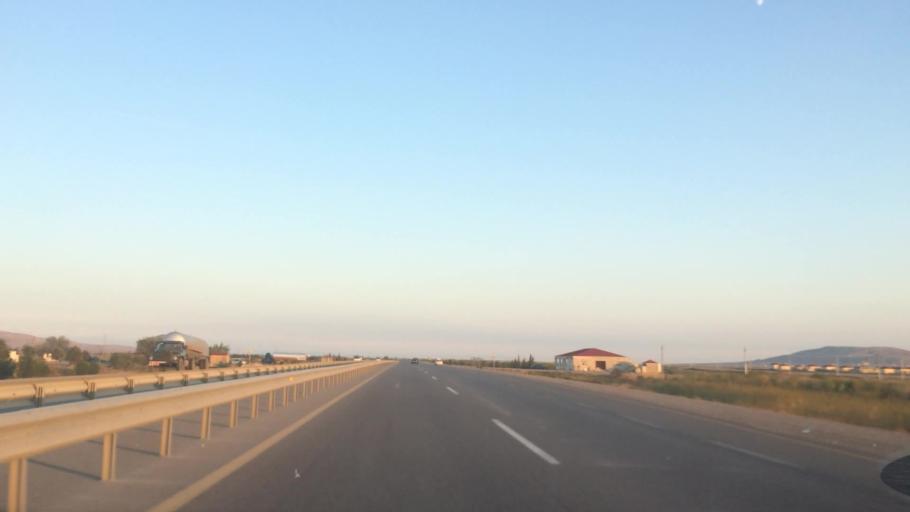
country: AZ
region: Baki
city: Qobustan
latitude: 39.9859
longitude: 49.2089
